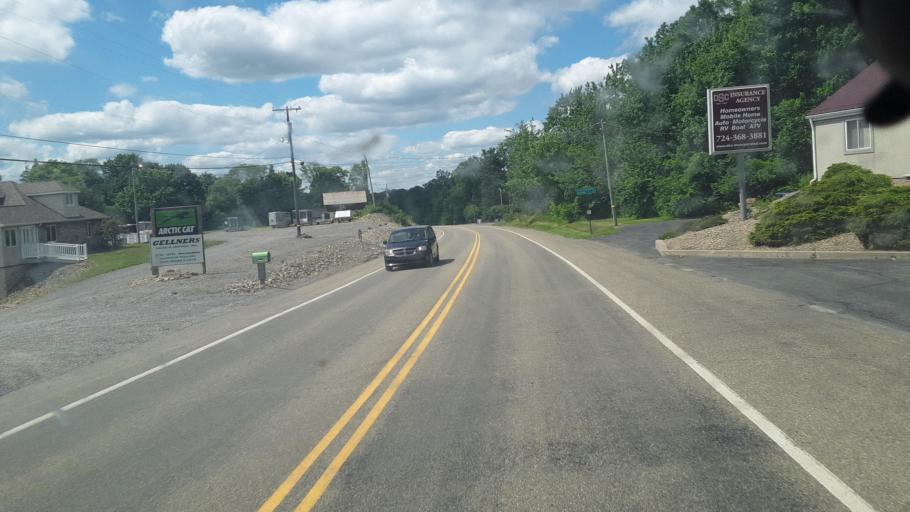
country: US
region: Pennsylvania
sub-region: Butler County
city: Prospect
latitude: 40.9330
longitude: -80.1464
